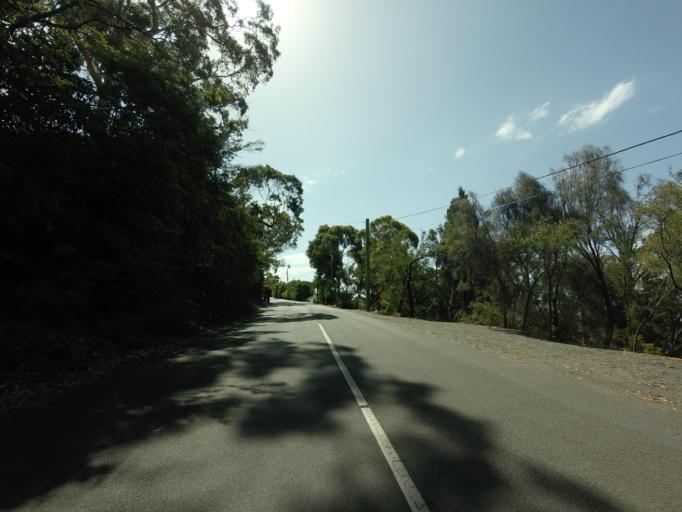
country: AU
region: Tasmania
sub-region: Hobart
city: Dynnyrne
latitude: -42.9111
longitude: 147.3276
